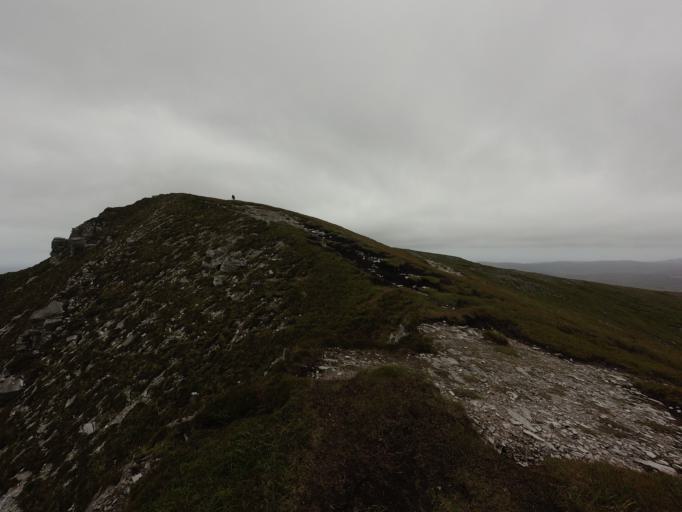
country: IE
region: Ulster
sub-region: County Donegal
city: Killybegs
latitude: 54.6468
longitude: -8.6900
